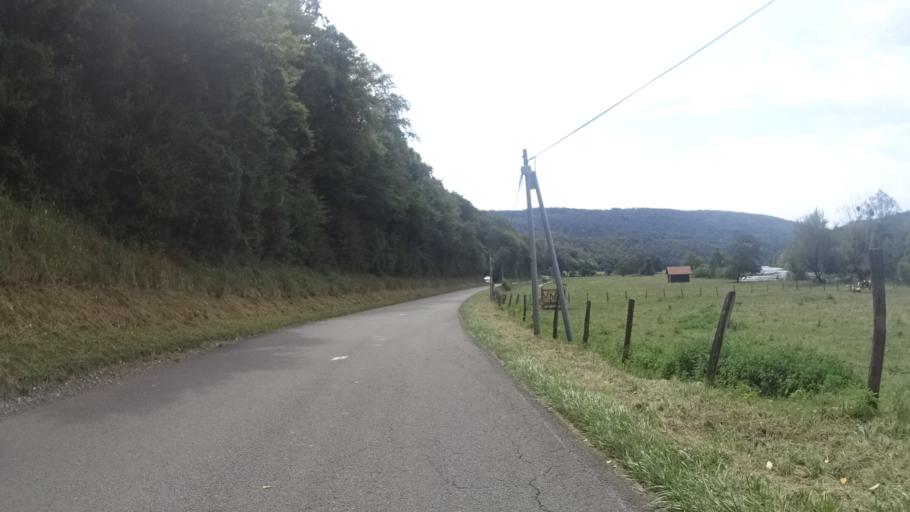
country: FR
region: Franche-Comte
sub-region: Departement du Doubs
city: Clerval
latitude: 47.3775
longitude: 6.5041
